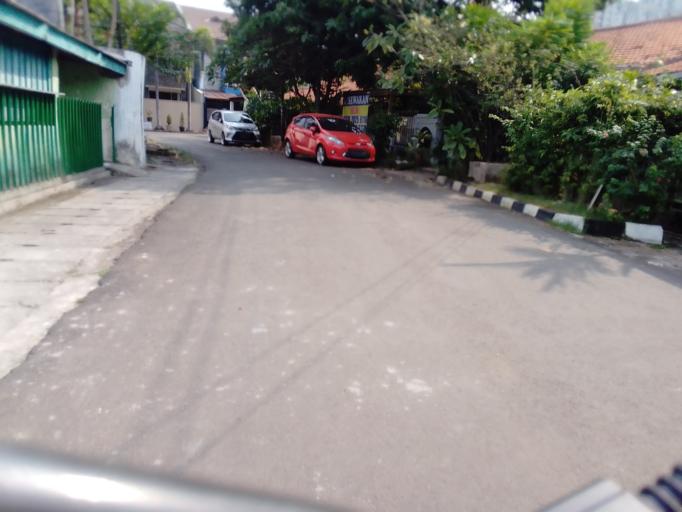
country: ID
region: Jakarta Raya
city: Jakarta
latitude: -6.2029
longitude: 106.8104
